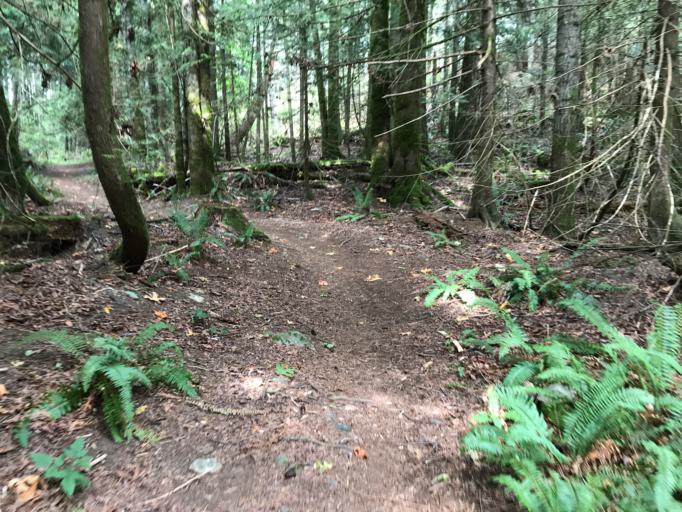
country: CA
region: British Columbia
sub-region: Cowichan Valley Regional District
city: Ladysmith
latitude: 48.9279
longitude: -123.7414
